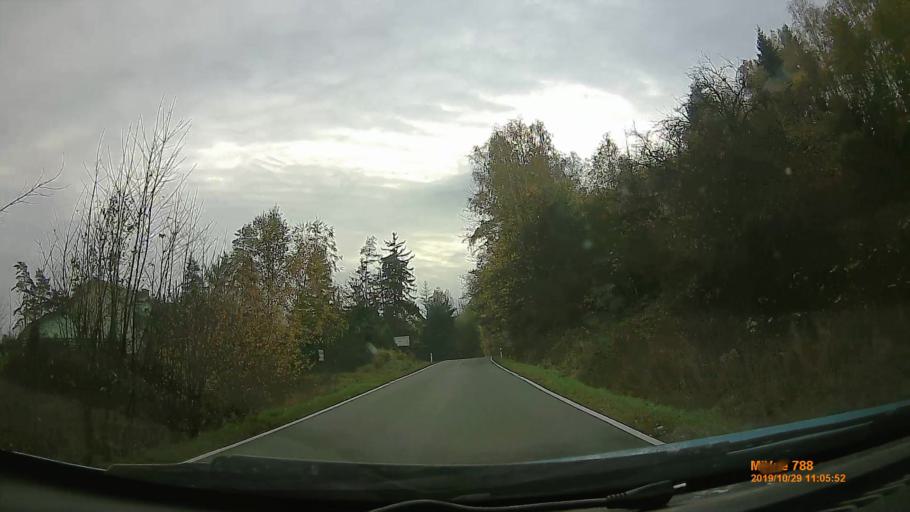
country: PL
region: Lower Silesian Voivodeship
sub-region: Powiat klodzki
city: Szczytna
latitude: 50.4672
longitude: 16.4779
